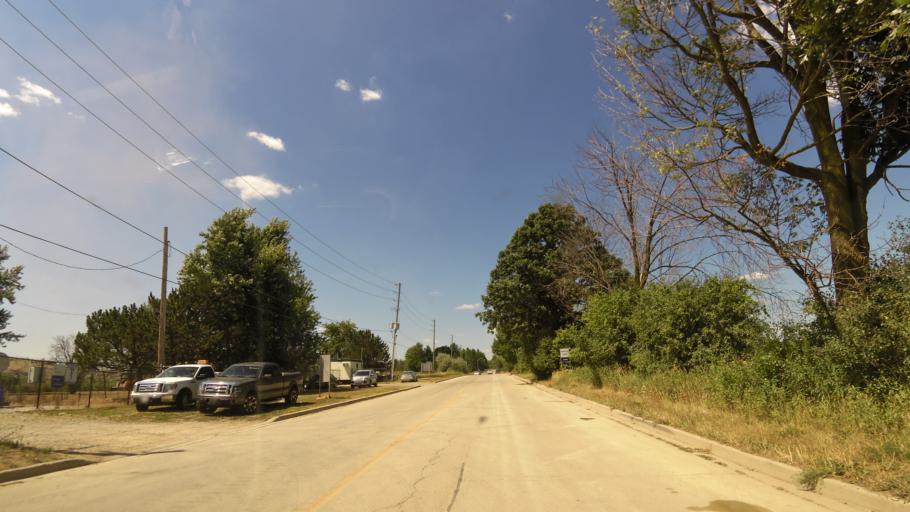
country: CA
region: Ontario
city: Brampton
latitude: 43.6389
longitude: -79.8640
